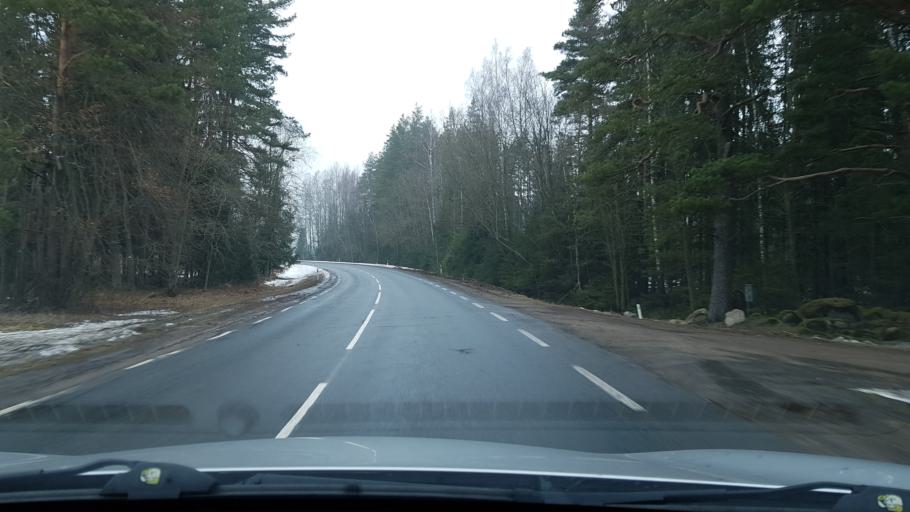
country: EE
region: Valgamaa
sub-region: Torva linn
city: Torva
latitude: 58.2051
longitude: 25.9503
